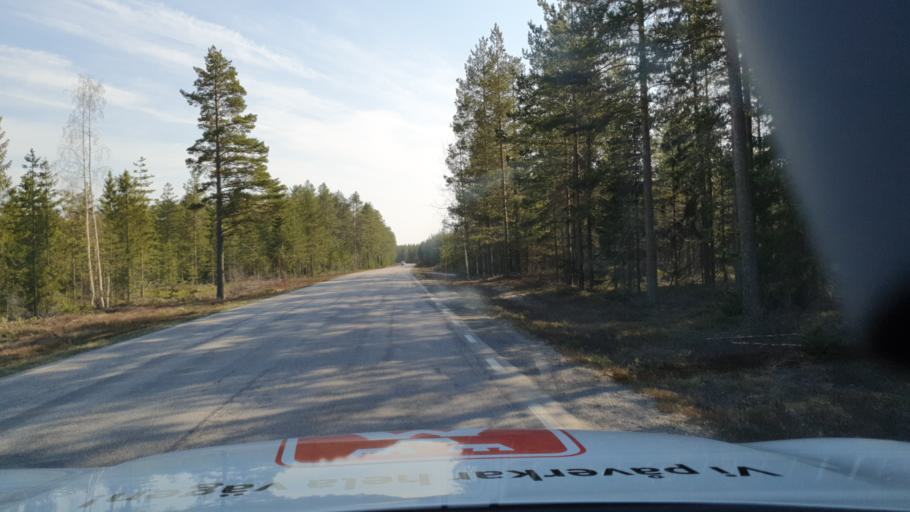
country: SE
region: Vaesterbotten
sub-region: Umea Kommun
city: Roback
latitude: 63.8717
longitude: 20.1493
